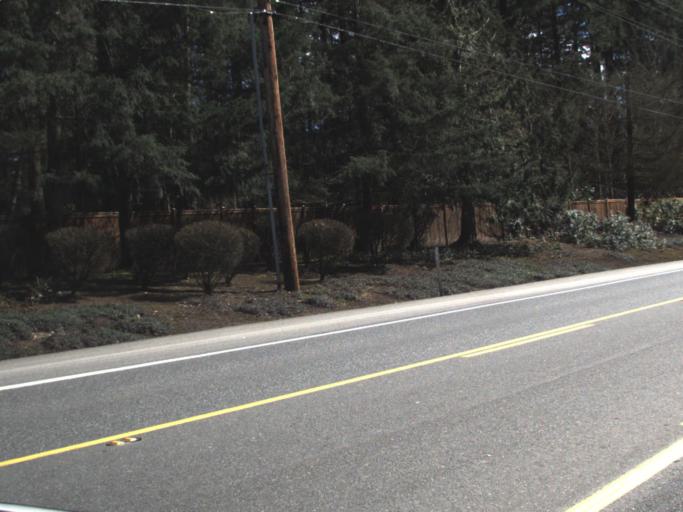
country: US
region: Washington
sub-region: King County
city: Maple Valley
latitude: 47.3741
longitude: -122.0242
